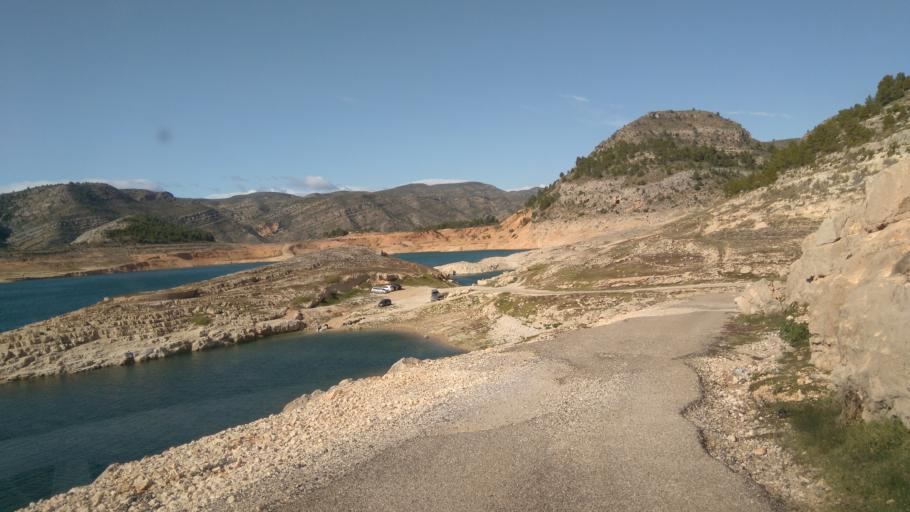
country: ES
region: Valencia
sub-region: Provincia de Valencia
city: Sumacarcer
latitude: 39.1532
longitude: -0.6566
